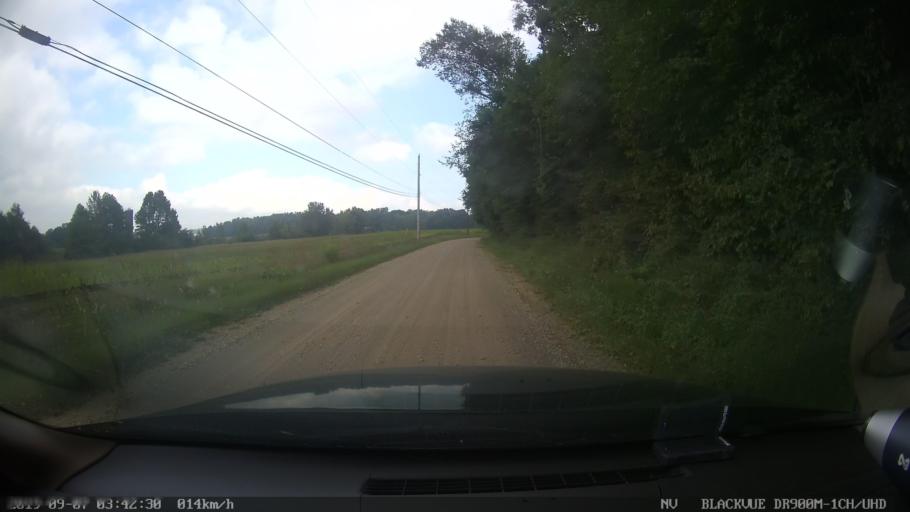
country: US
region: Ohio
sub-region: Licking County
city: Granville
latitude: 40.1226
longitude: -82.5476
